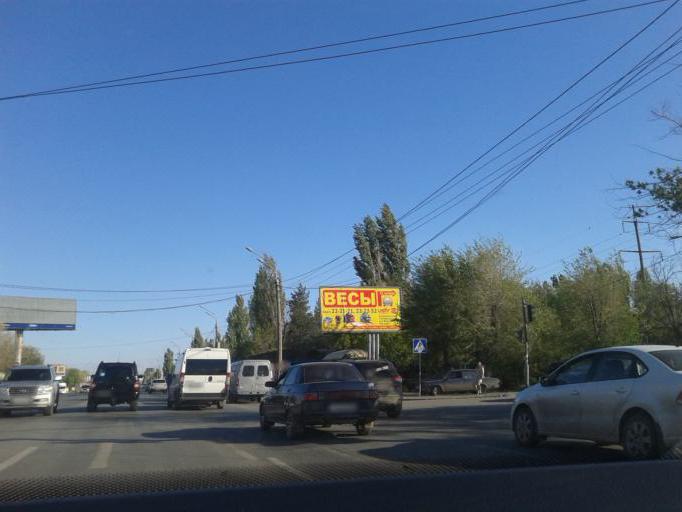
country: RU
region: Volgograd
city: Gorodishche
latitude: 48.7617
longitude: 44.4770
